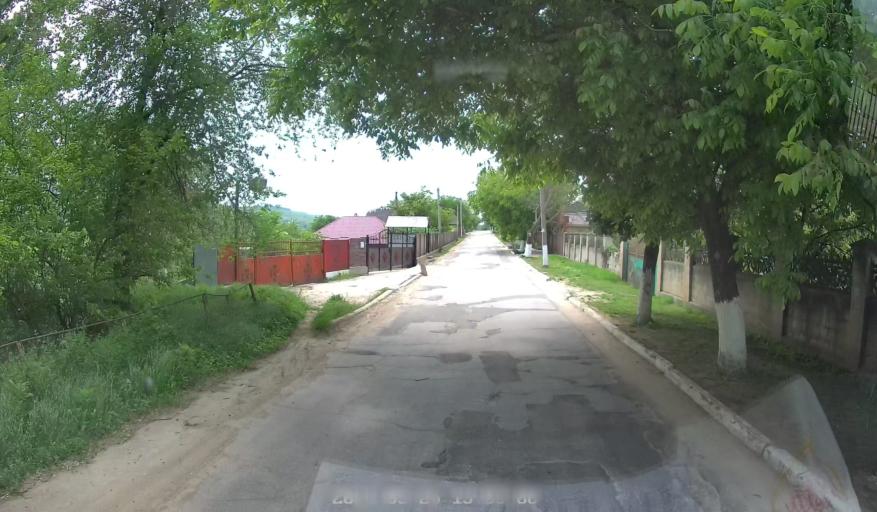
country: MD
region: Hincesti
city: Dancu
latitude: 46.7640
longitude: 28.3449
